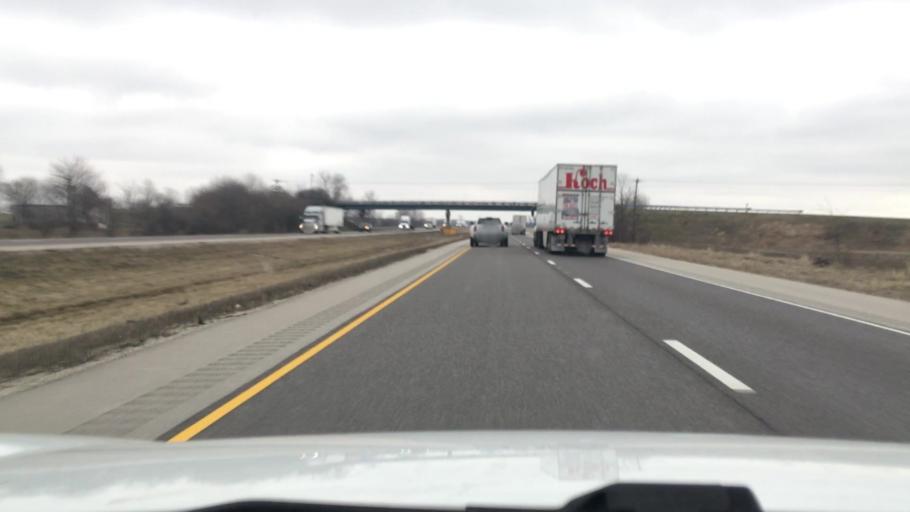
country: US
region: Illinois
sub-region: Fayette County
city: Saint Elmo
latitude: 39.0257
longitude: -88.8081
